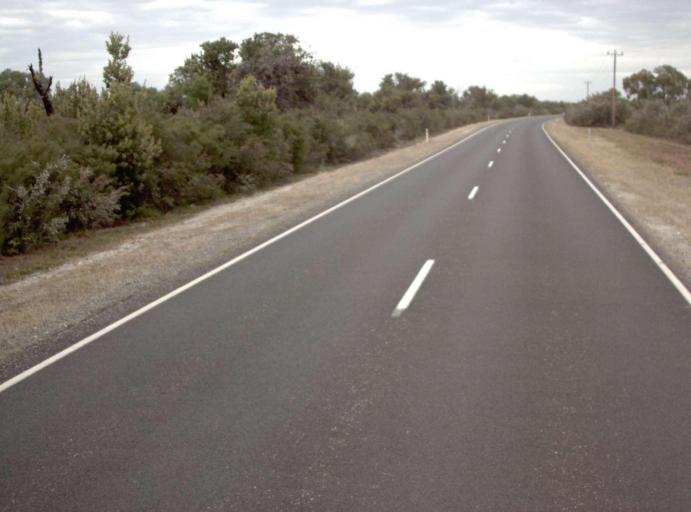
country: AU
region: Victoria
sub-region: Wellington
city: Sale
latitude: -38.1877
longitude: 147.3701
